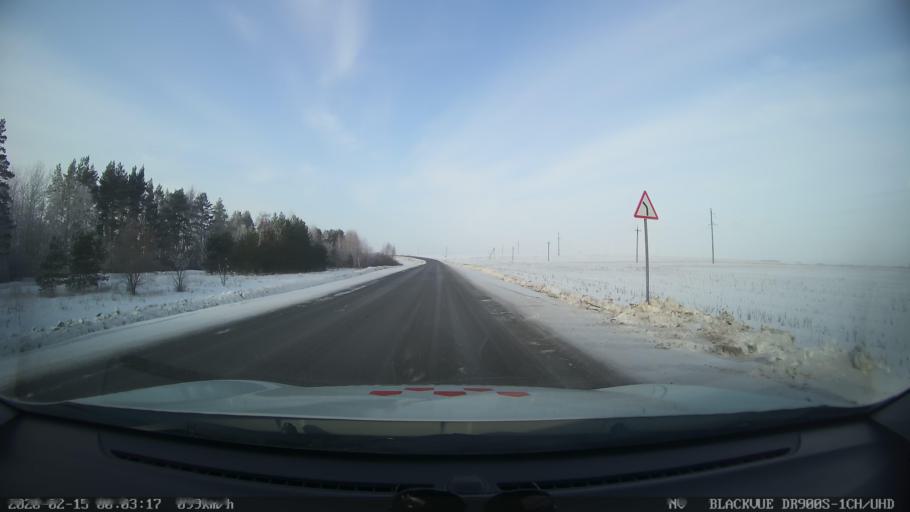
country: RU
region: Tatarstan
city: Kuybyshevskiy Zaton
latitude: 55.3697
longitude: 48.9988
